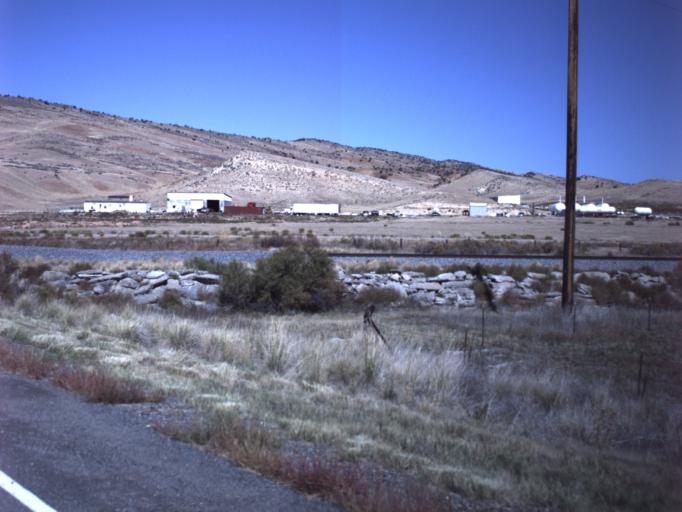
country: US
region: Utah
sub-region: Juab County
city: Nephi
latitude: 39.4853
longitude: -111.9815
